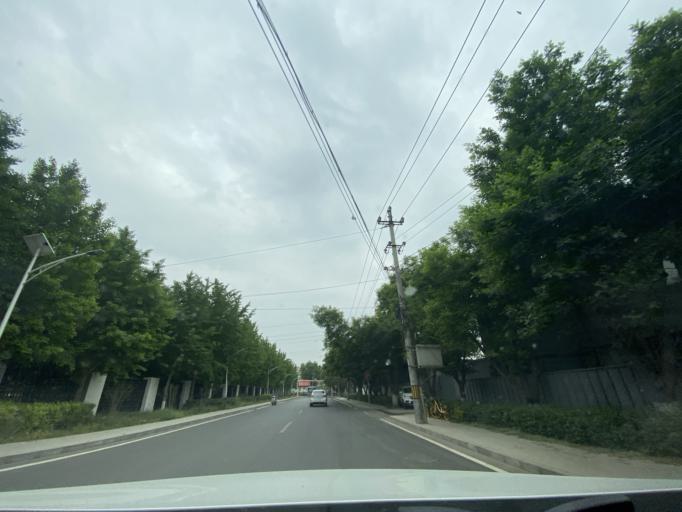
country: CN
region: Beijing
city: Sijiqing
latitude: 39.9348
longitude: 116.2390
